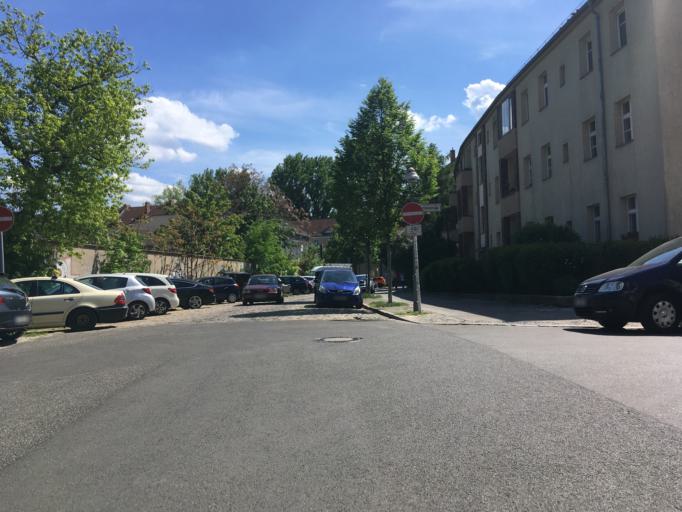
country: DE
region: Berlin
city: Berlin Koepenick
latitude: 52.4563
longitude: 13.5857
